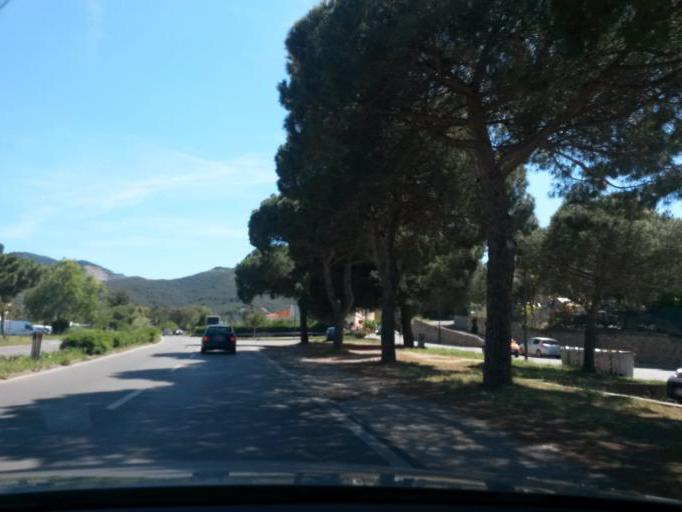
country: IT
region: Tuscany
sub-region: Provincia di Livorno
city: Portoferraio
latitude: 42.8075
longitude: 10.3086
